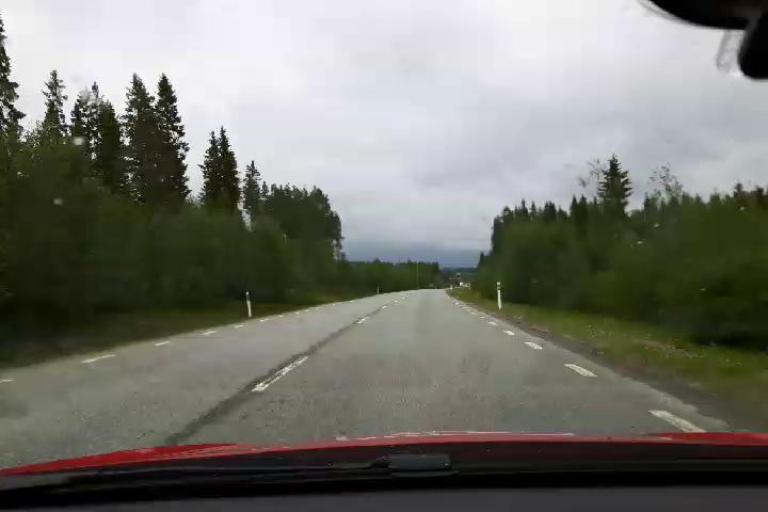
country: SE
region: Jaemtland
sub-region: Bergs Kommun
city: Hoverberg
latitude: 62.6751
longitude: 14.3835
